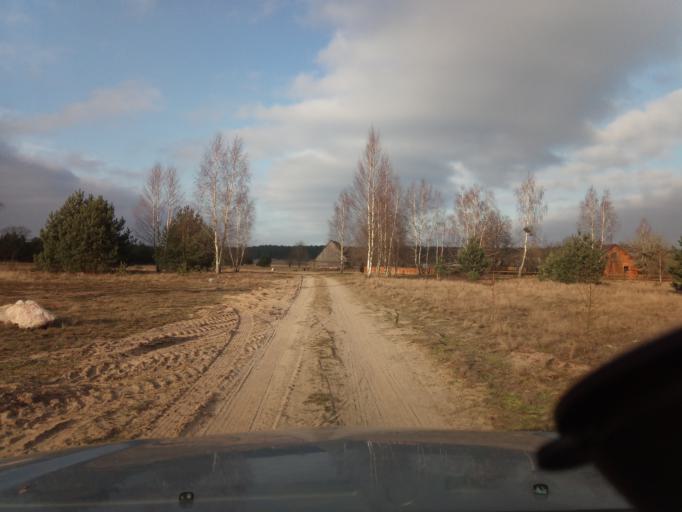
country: LT
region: Alytaus apskritis
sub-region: Alytaus rajonas
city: Daugai
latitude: 54.1144
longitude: 24.2378
